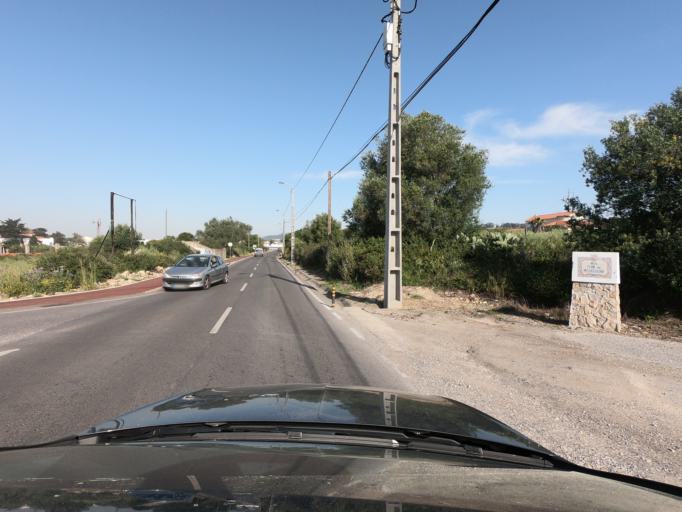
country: PT
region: Lisbon
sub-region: Cascais
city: Parede
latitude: 38.7367
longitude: -9.3567
